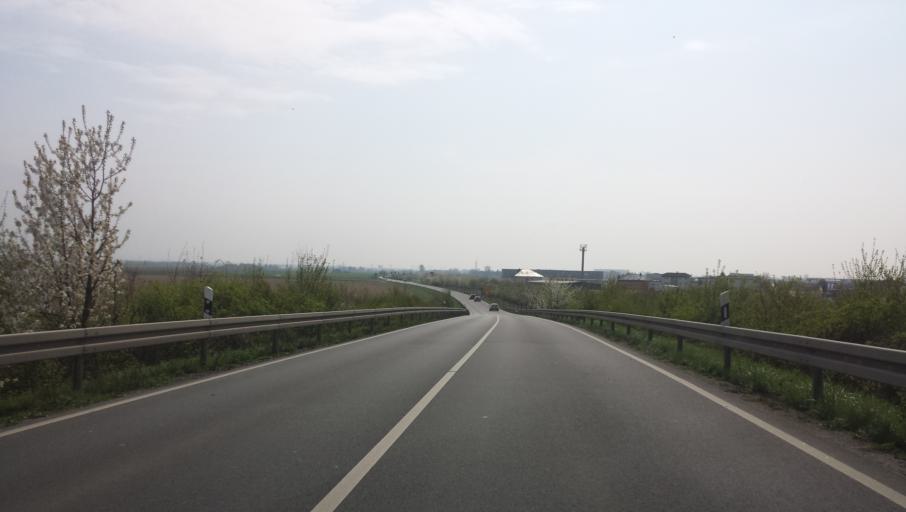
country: DE
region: Hesse
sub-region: Regierungsbezirk Darmstadt
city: Stockstadt am Rhein
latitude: 49.8190
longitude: 8.4805
